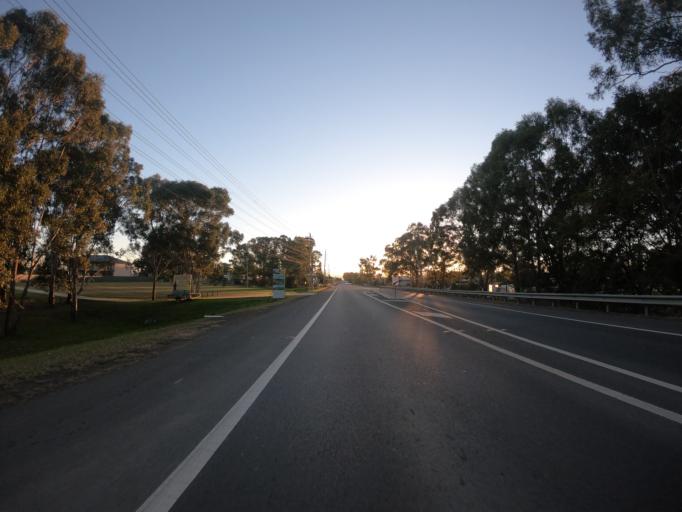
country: AU
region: New South Wales
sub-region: Hawkesbury
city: South Windsor
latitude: -33.6310
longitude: 150.7922
